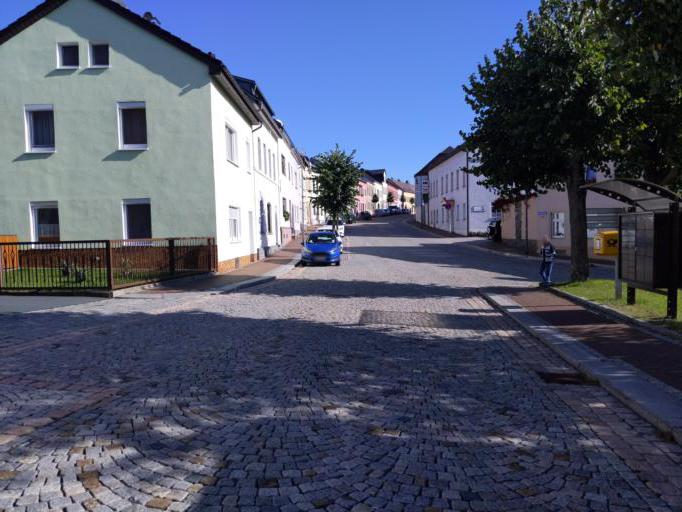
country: DE
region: Saxony
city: Pohl
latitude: 50.3929
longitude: 12.3302
